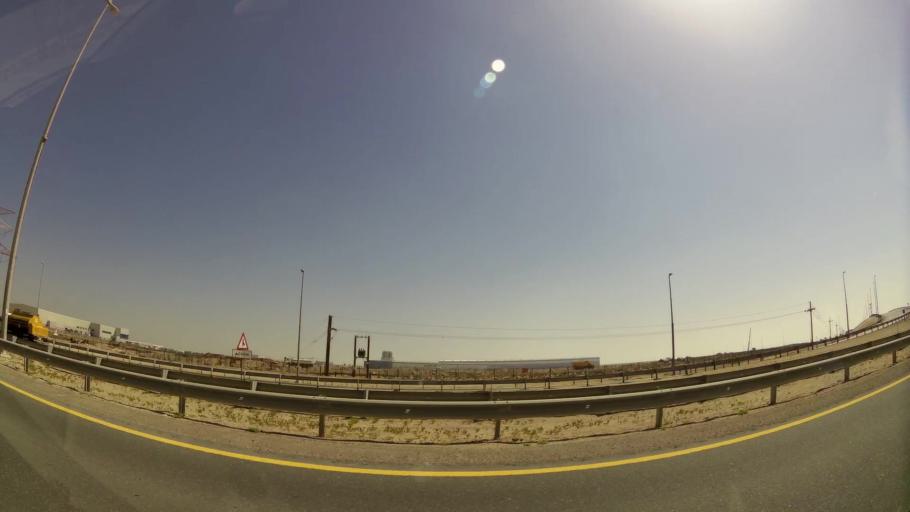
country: AE
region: Dubai
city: Dubai
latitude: 24.9215
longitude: 55.1007
